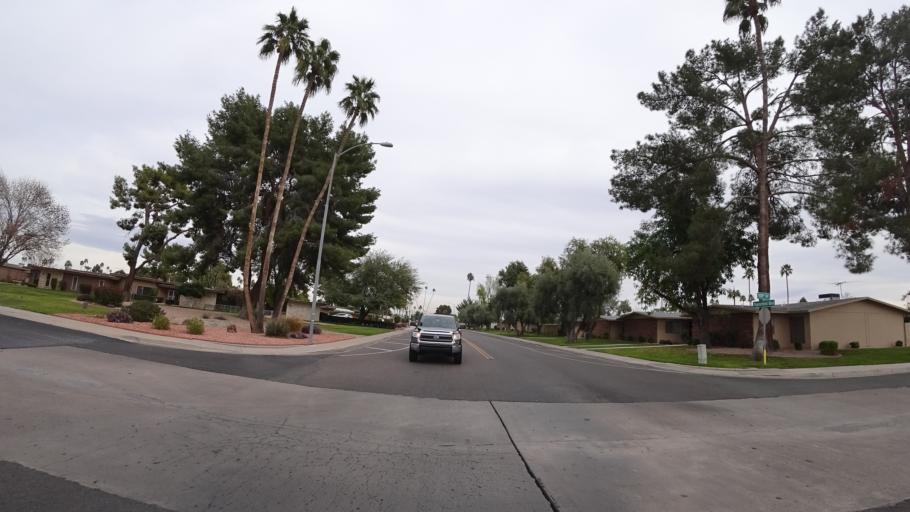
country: US
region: Arizona
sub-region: Maricopa County
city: Youngtown
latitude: 33.6065
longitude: -112.2930
